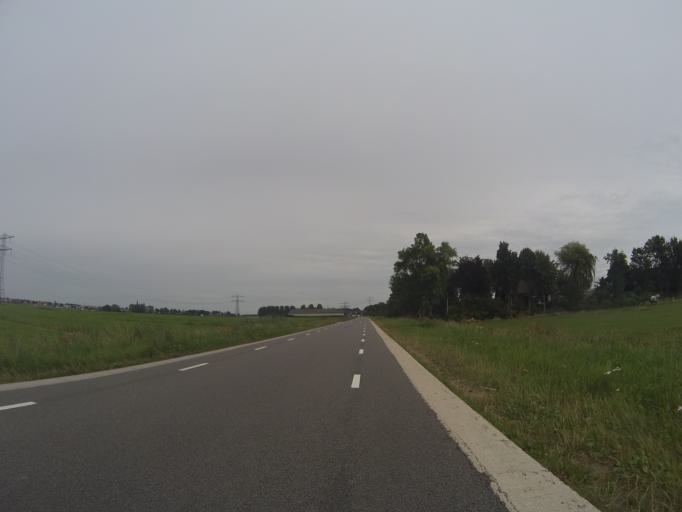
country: NL
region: Utrecht
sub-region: Gemeente Bunschoten
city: Bunschoten
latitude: 52.2432
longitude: 5.3934
